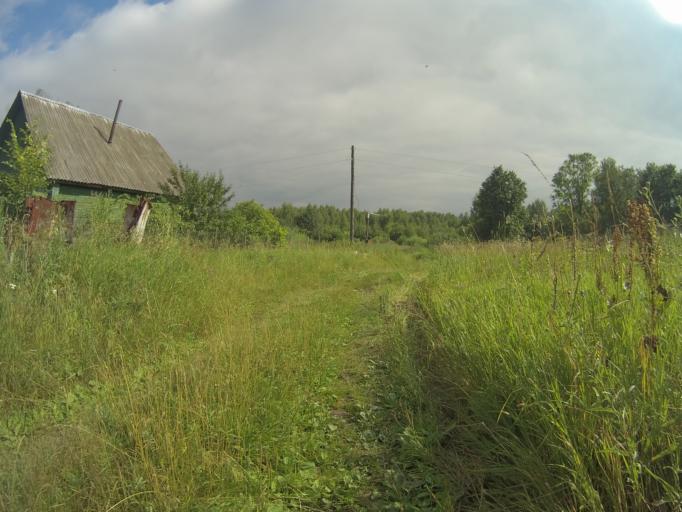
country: RU
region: Vladimir
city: Vorsha
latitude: 56.0042
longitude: 40.2002
